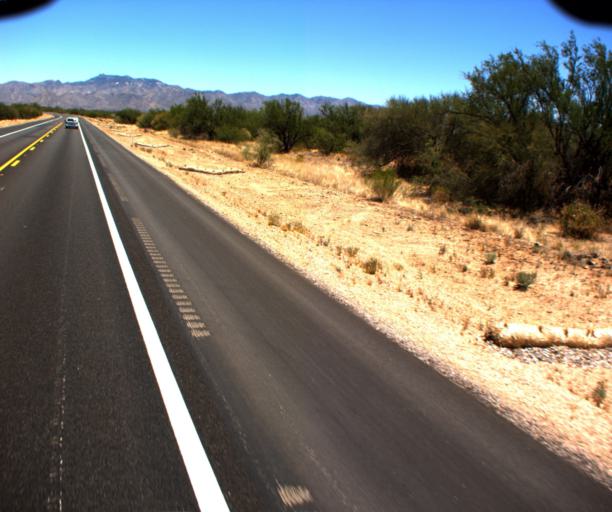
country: US
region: Arizona
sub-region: Pima County
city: Sells
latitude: 31.9285
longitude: -111.7898
